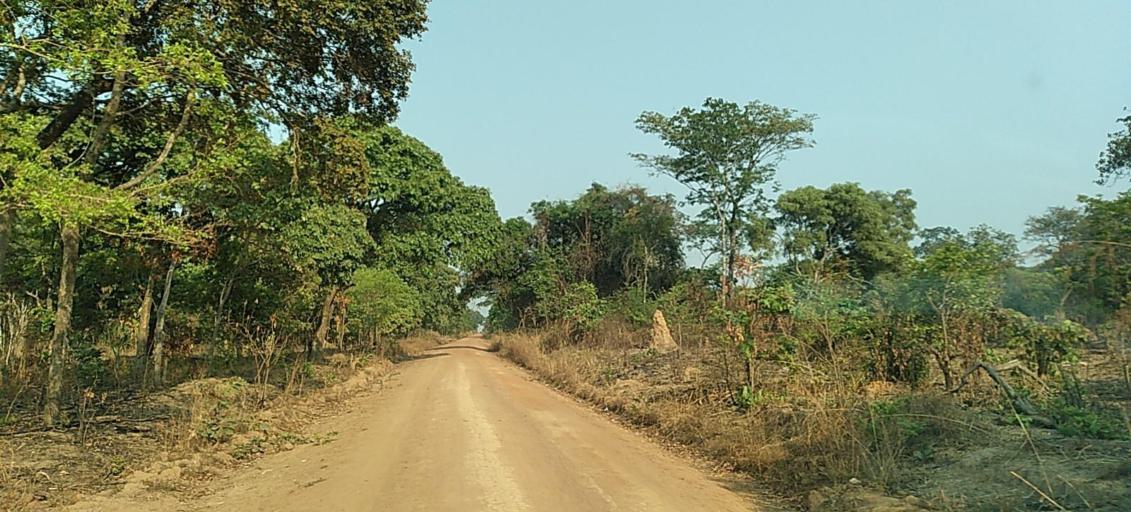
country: ZM
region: Copperbelt
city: Chingola
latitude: -12.8617
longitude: 27.5758
